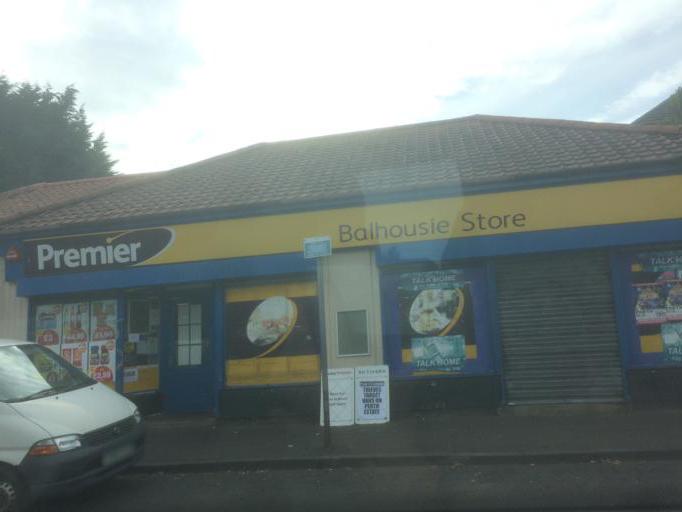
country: GB
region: Scotland
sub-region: Perth and Kinross
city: Perth
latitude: 56.4051
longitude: -3.4406
